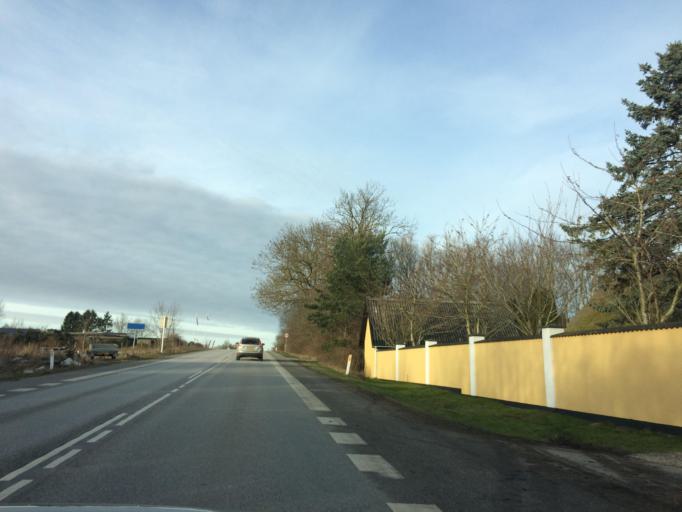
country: DK
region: Capital Region
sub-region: Fredensborg Kommune
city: Fredensborg
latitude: 55.9467
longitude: 12.4238
